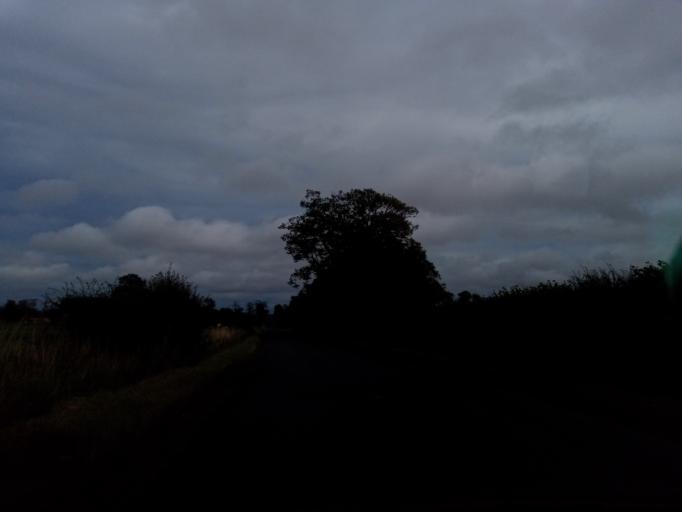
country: GB
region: Scotland
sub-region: The Scottish Borders
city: Duns
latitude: 55.7619
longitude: -2.3349
